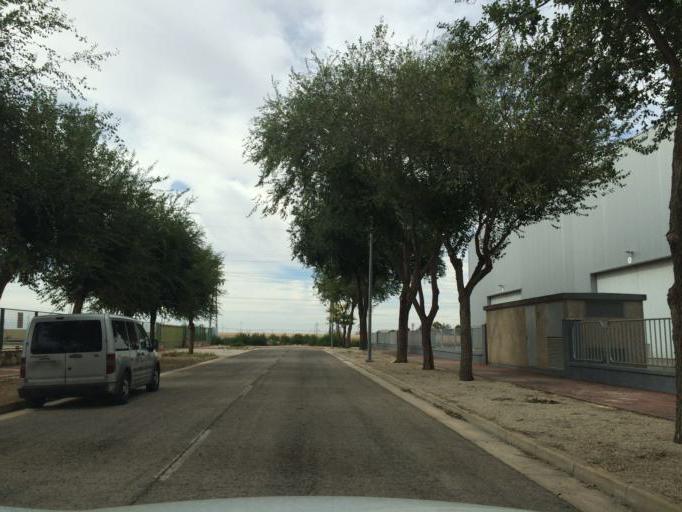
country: ES
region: Castille-La Mancha
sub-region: Provincia de Albacete
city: Albacete
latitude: 39.0217
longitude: -1.8903
